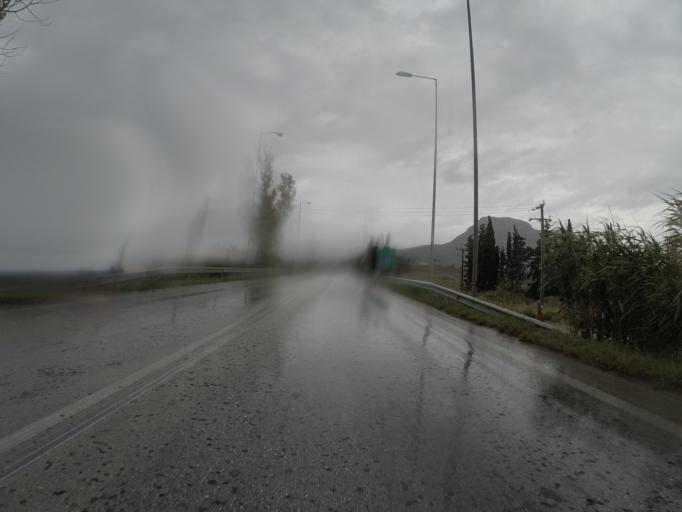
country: GR
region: Peloponnese
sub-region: Nomos Korinthias
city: Arkhaia Korinthos
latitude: 37.9179
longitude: 22.8844
